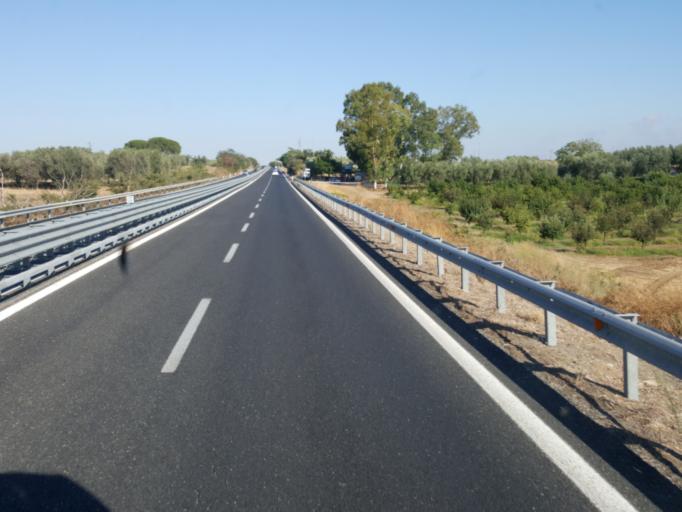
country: IT
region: Latium
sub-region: Provincia di Viterbo
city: Pescia Romana
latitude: 42.3936
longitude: 11.5300
